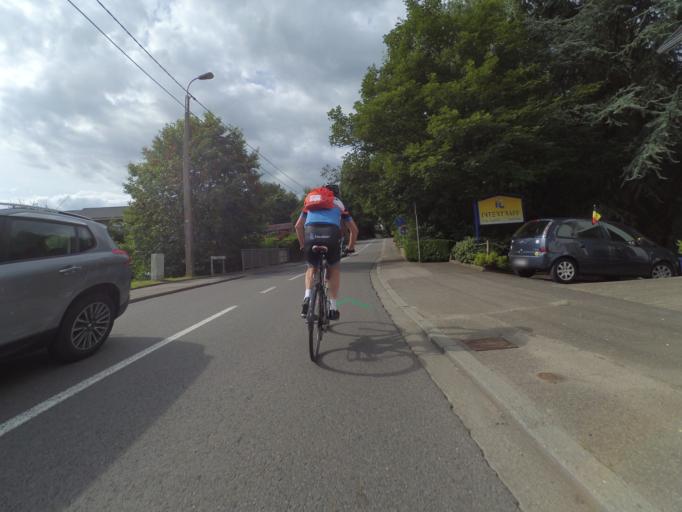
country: BE
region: Wallonia
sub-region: Province de Liege
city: La Calamine
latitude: 50.7136
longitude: 6.0183
